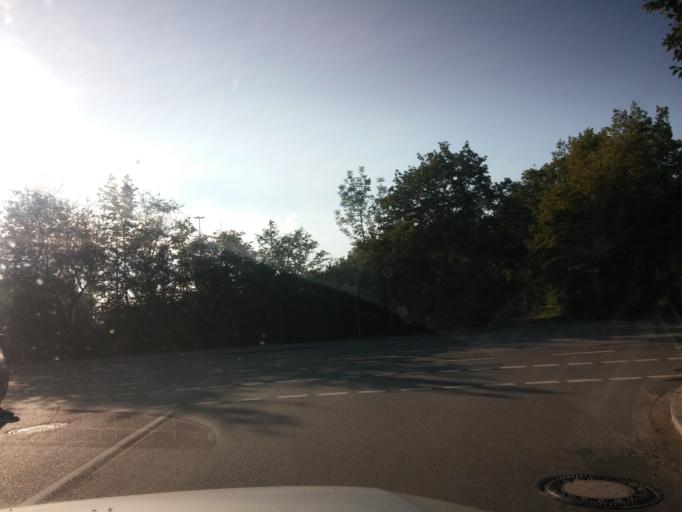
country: DE
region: Bavaria
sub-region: Upper Bavaria
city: Feldkirchen
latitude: 48.1523
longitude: 11.7405
